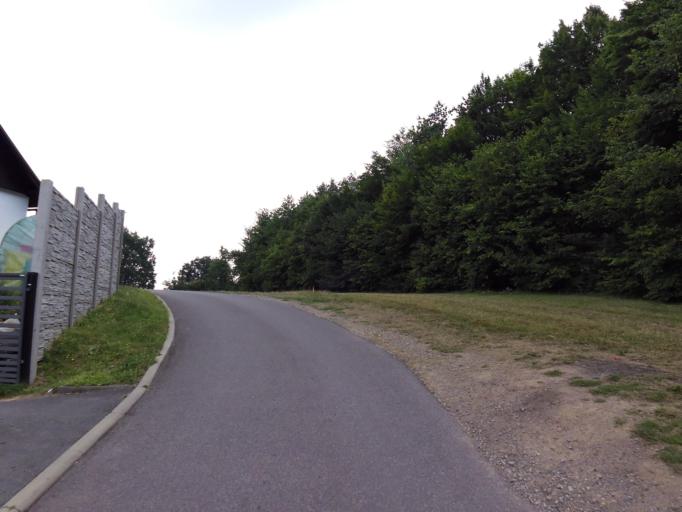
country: CZ
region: Central Bohemia
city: Kamenice
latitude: 49.8906
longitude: 14.6132
